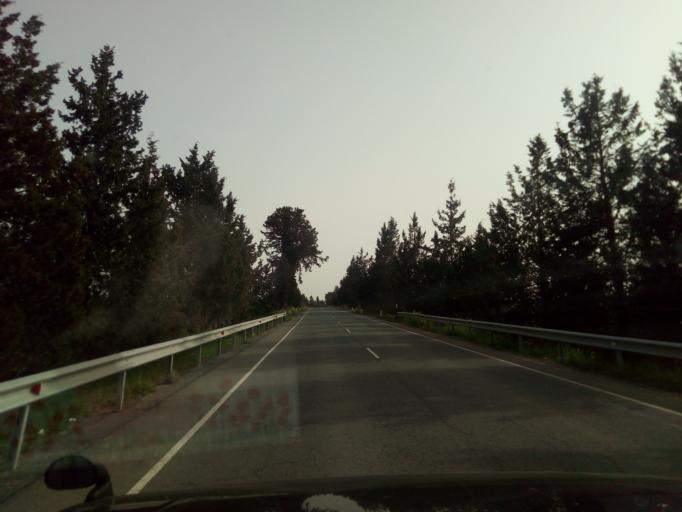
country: CY
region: Lefkosia
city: Lympia
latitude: 35.0161
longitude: 33.4959
